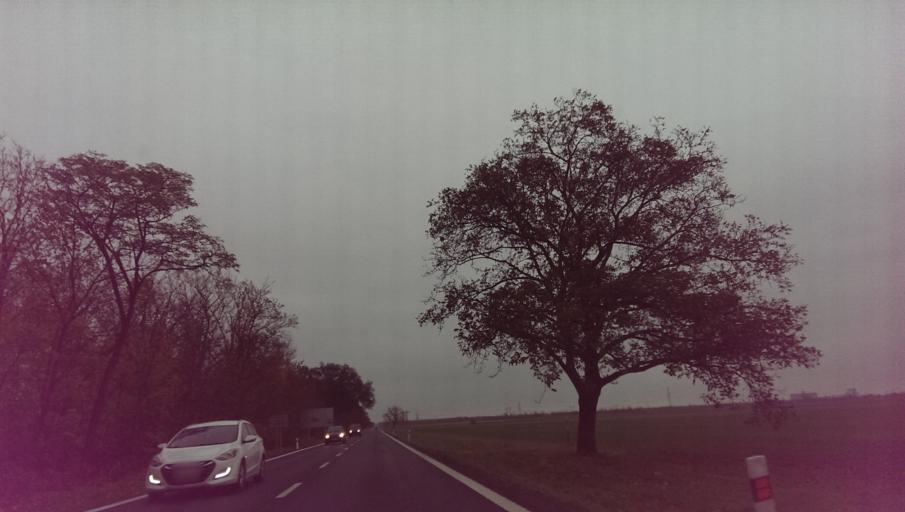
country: CZ
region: South Moravian
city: Suchohrdly
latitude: 48.8549
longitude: 16.1153
